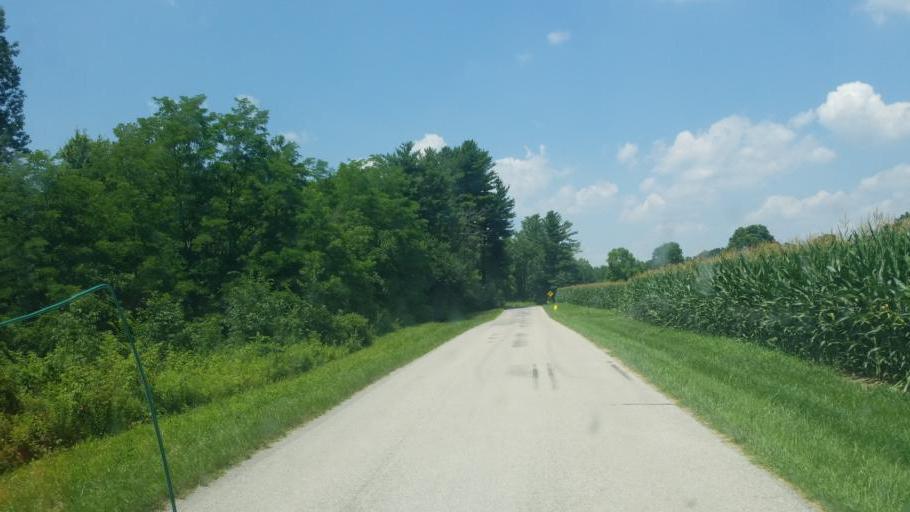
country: US
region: Ohio
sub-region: Richland County
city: Shelby
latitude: 40.8590
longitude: -82.6593
